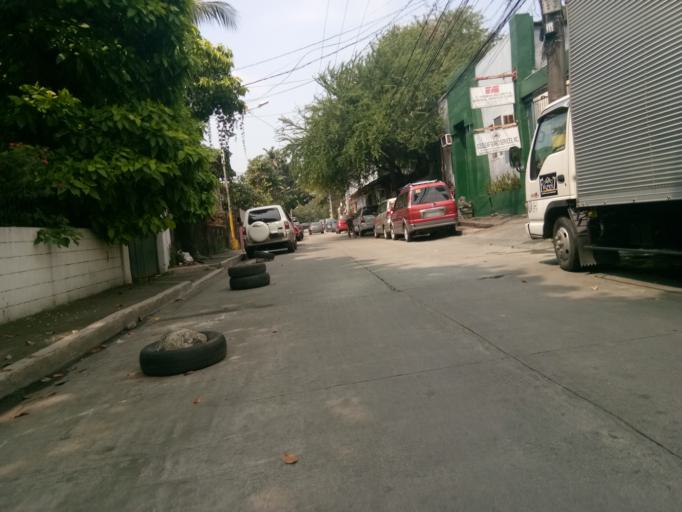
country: PH
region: Metro Manila
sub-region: San Juan
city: San Juan
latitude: 14.6118
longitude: 121.0537
